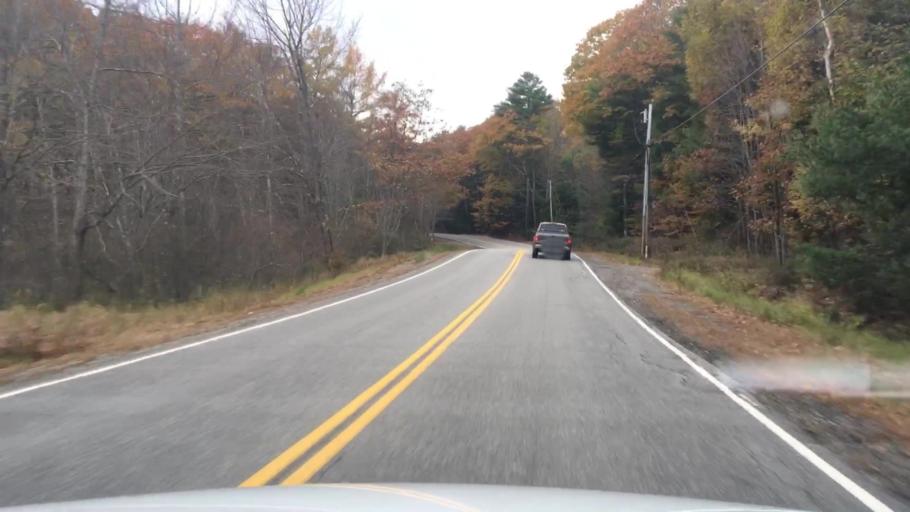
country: US
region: Maine
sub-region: Androscoggin County
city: Sabattus
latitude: 44.1323
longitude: -70.0325
